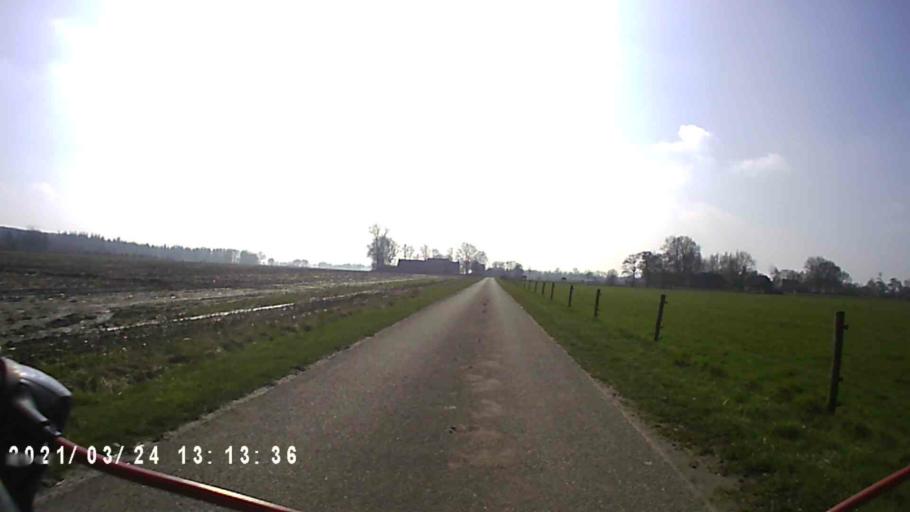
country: NL
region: Groningen
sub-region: Gemeente Leek
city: Leek
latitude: 53.1195
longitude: 6.2924
